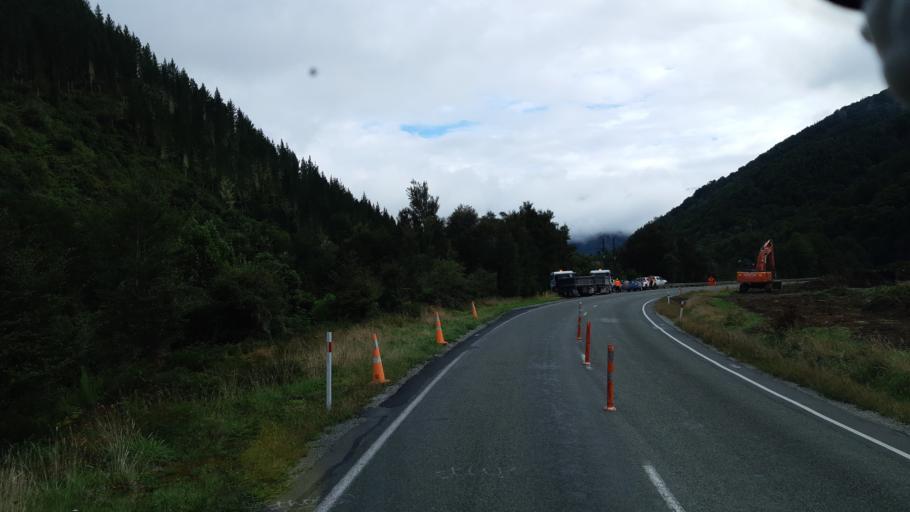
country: NZ
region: West Coast
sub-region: Buller District
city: Westport
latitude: -41.9613
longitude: 172.2001
